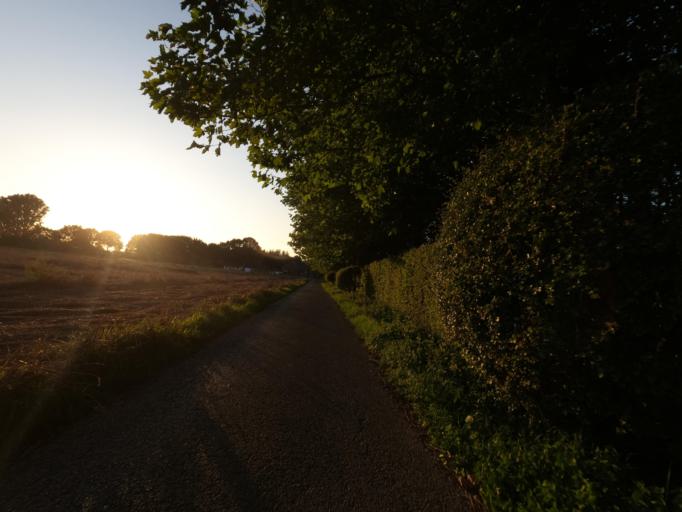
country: DE
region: North Rhine-Westphalia
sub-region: Regierungsbezirk Koln
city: Linnich
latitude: 51.0082
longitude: 6.2730
